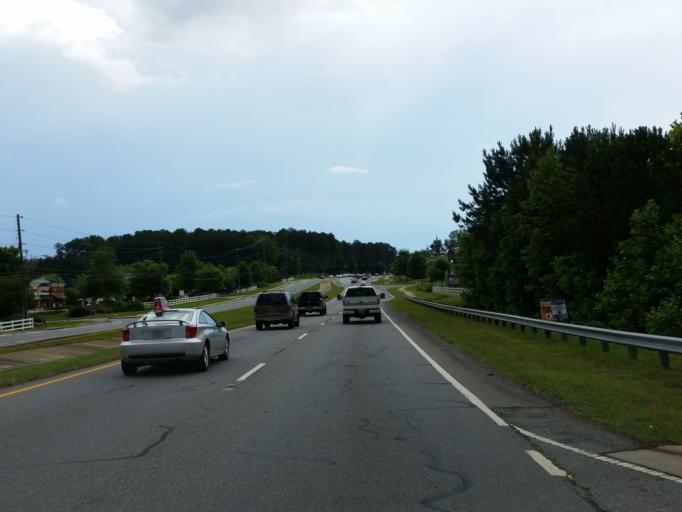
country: US
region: Georgia
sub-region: Cherokee County
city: Woodstock
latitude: 34.0877
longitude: -84.4703
